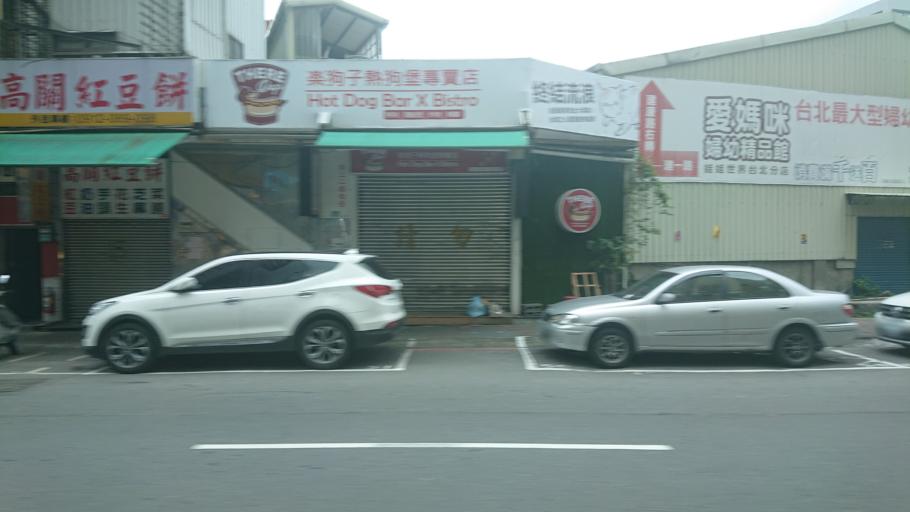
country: TW
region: Taipei
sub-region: Taipei
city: Banqiao
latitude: 24.9979
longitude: 121.4883
